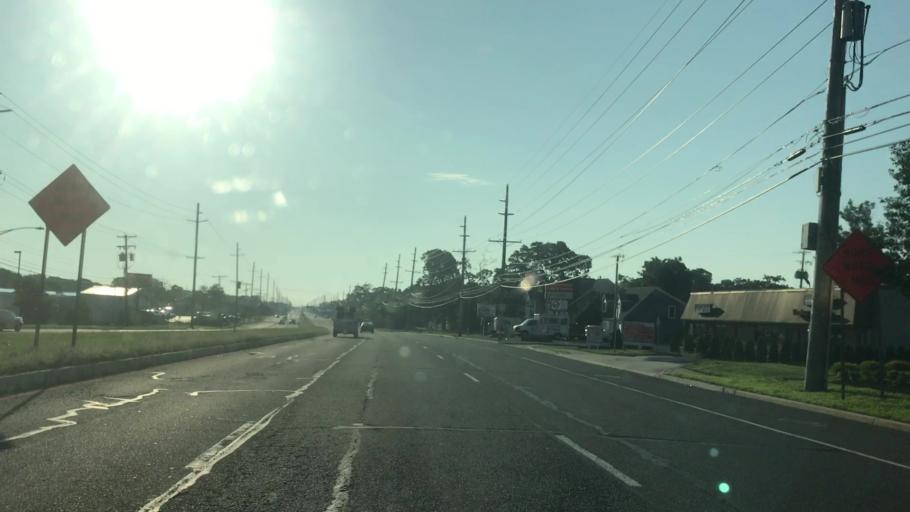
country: US
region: New Jersey
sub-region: Ocean County
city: Island Heights
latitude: 39.9512
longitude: -74.1467
